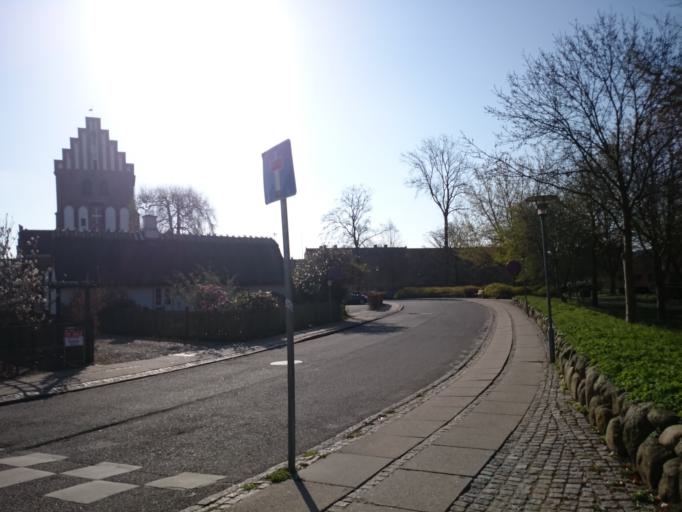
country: DK
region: Capital Region
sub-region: Rudersdal Kommune
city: Birkerod
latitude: 55.8409
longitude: 12.4283
